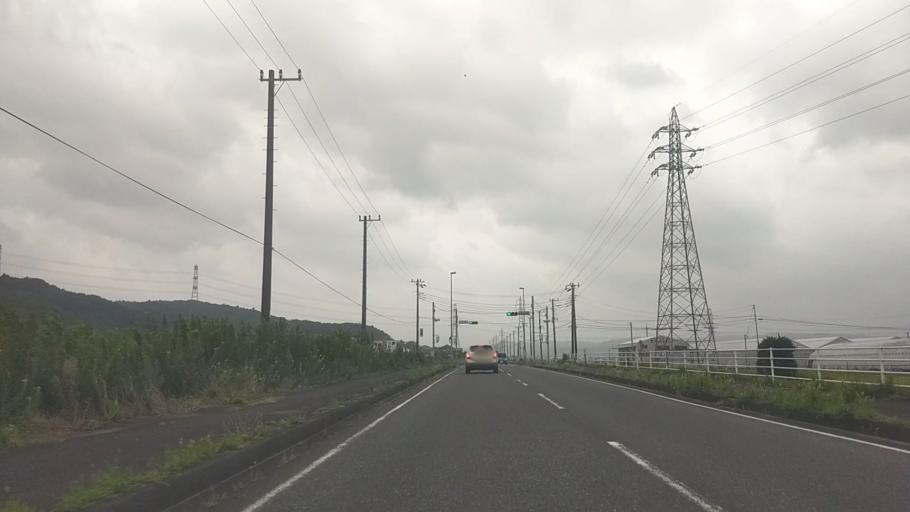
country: JP
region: Chiba
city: Kisarazu
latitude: 35.3513
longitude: 140.0548
